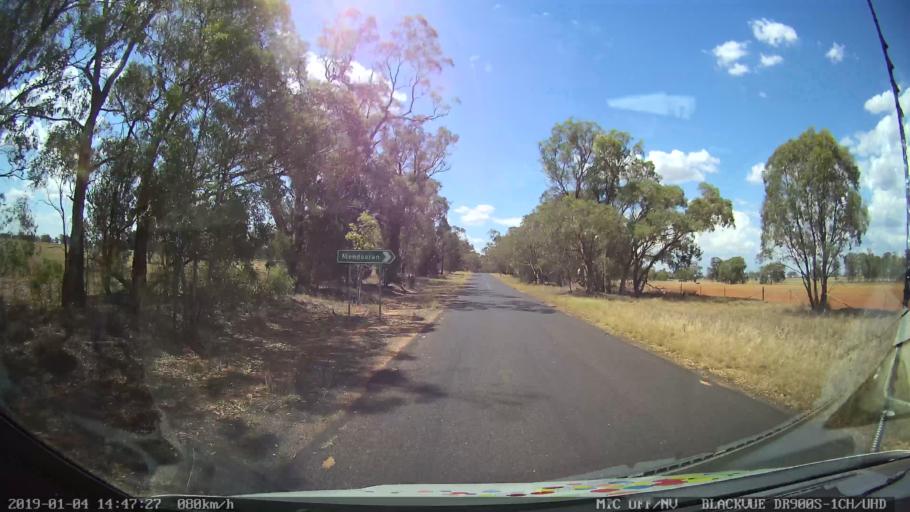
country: AU
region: New South Wales
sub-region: Dubbo Municipality
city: Dubbo
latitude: -32.0690
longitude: 148.6602
